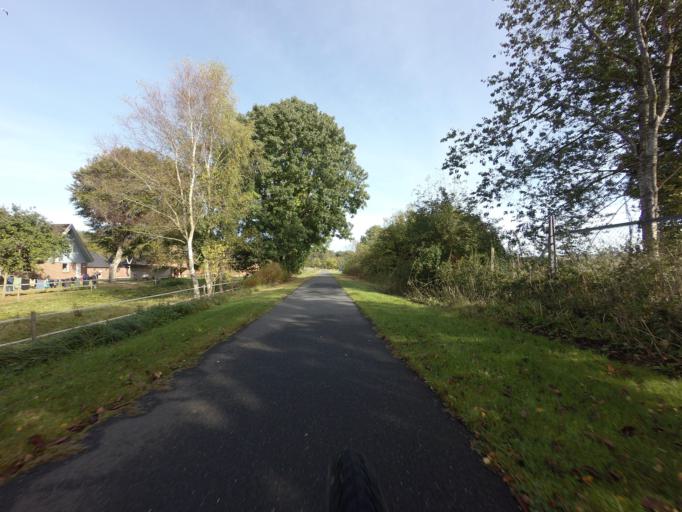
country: DK
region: Central Jutland
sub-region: Viborg Kommune
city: Viborg
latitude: 56.4267
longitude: 9.4545
